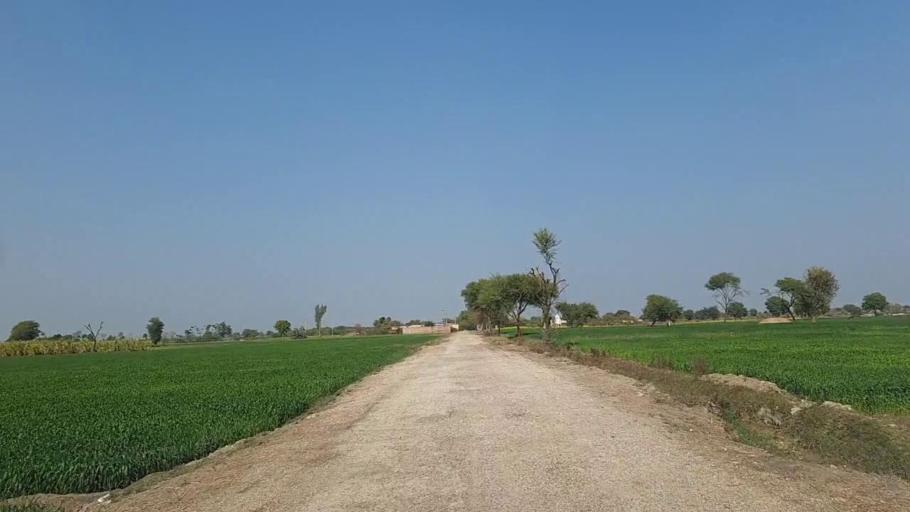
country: PK
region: Sindh
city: Jam Sahib
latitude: 26.2703
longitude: 68.5210
